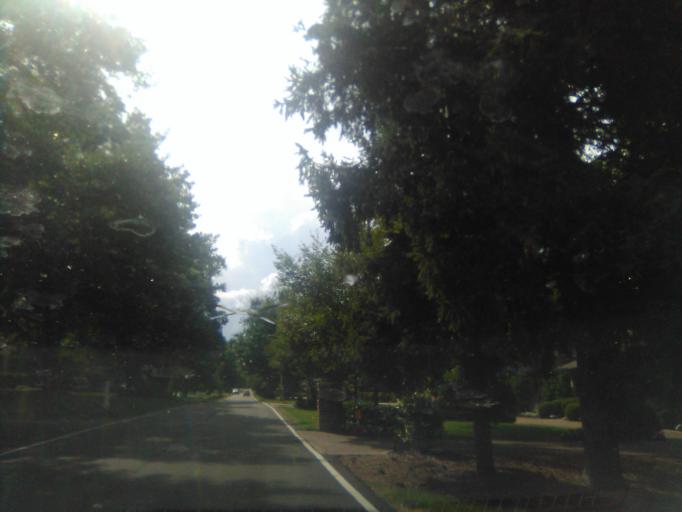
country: US
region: Tennessee
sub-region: Davidson County
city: Belle Meade
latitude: 36.0918
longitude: -86.8702
